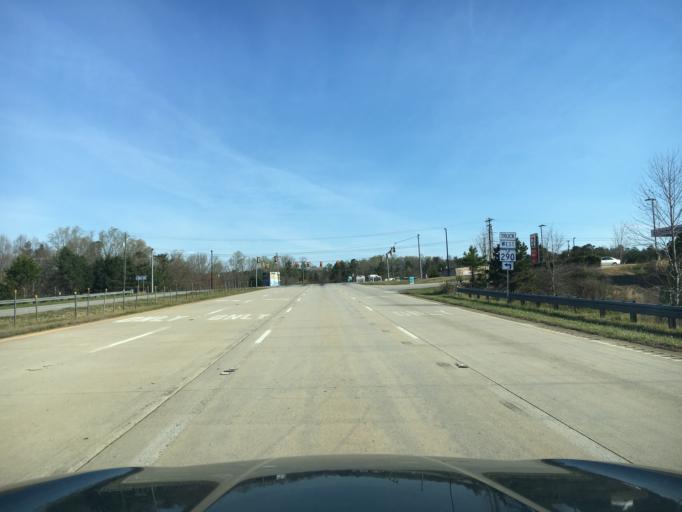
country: US
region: South Carolina
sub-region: Spartanburg County
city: Duncan
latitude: 34.9513
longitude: -82.1797
